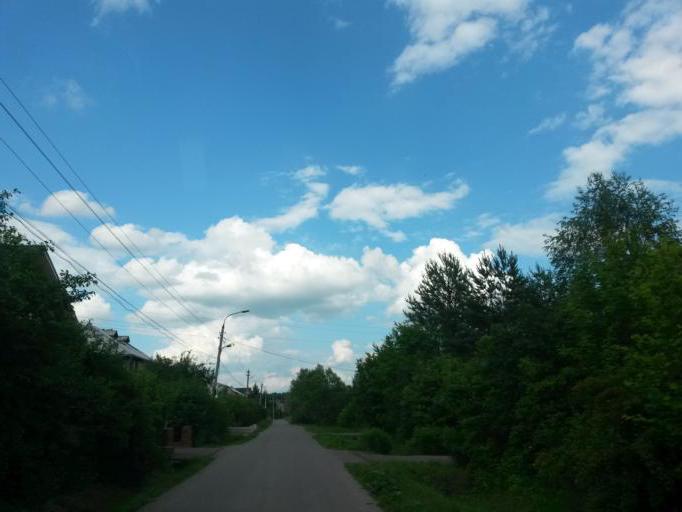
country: RU
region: Moskovskaya
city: Lyubuchany
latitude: 55.2660
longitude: 37.5583
